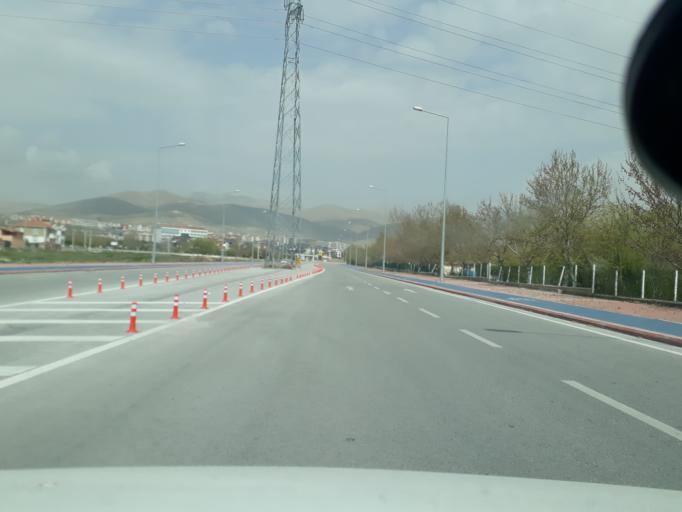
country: TR
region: Konya
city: Sille
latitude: 37.9469
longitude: 32.4794
